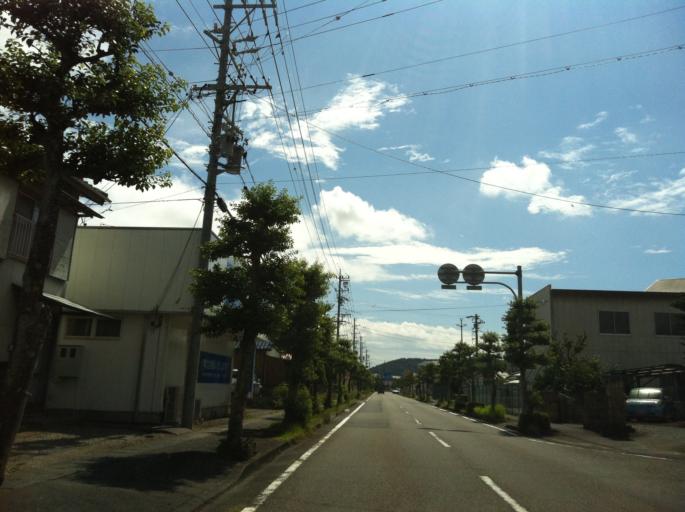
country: JP
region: Shizuoka
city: Kanaya
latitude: 34.8303
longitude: 138.1289
